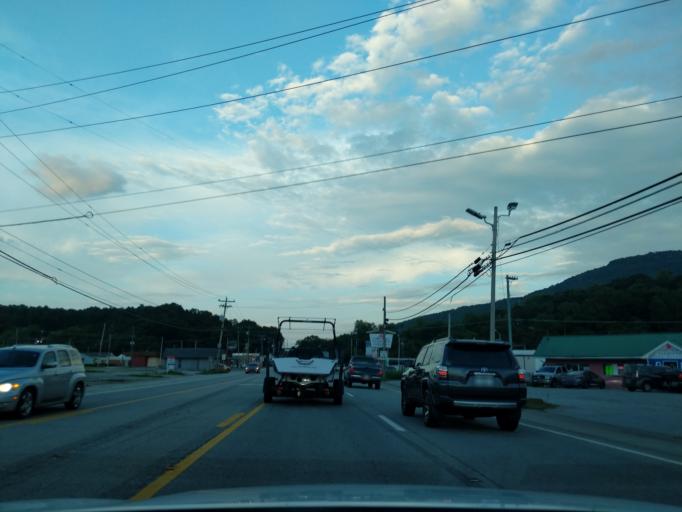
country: US
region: Tennessee
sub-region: Hamilton County
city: Lookout Mountain
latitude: 35.0198
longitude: -85.3688
